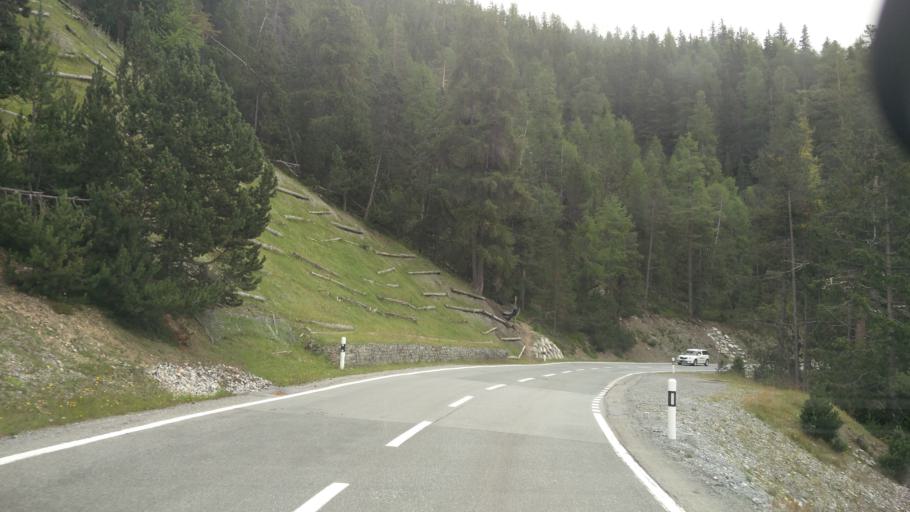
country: CH
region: Grisons
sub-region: Inn District
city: Zernez
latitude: 46.6733
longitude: 10.1681
